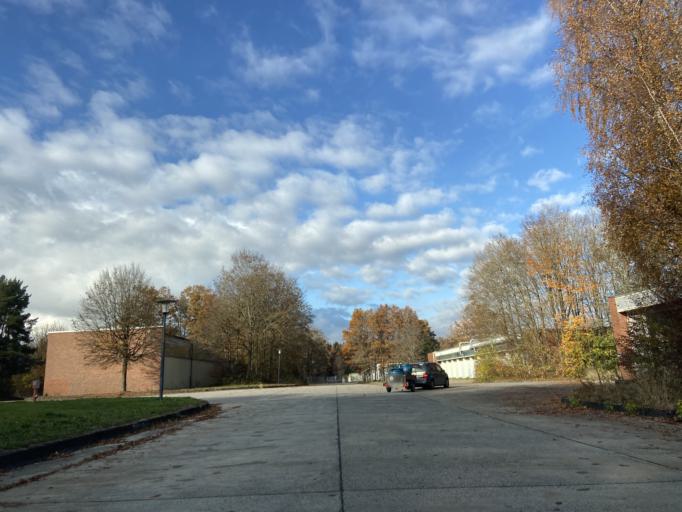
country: DE
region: Baden-Wuerttemberg
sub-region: Tuebingen Region
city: Sigmaringen
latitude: 48.0929
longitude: 9.2502
